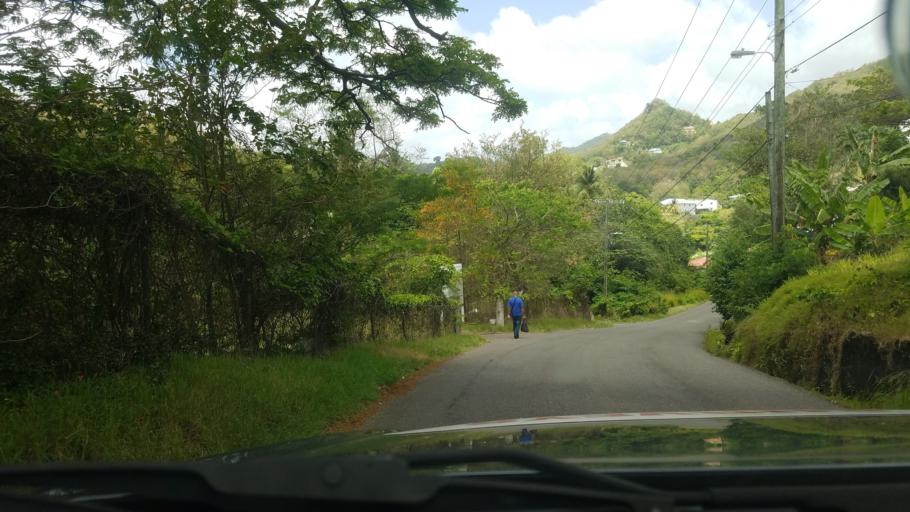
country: LC
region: Gros-Islet
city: Gros Islet
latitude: 14.0609
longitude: -60.9520
